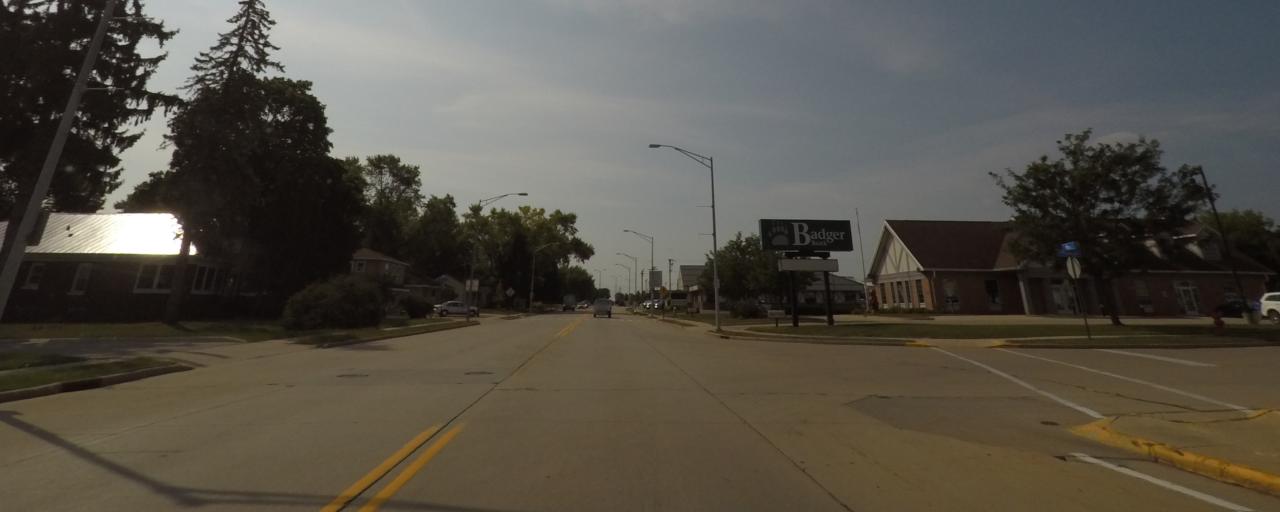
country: US
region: Wisconsin
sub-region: Jefferson County
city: Jefferson
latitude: 42.9948
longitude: -88.8073
